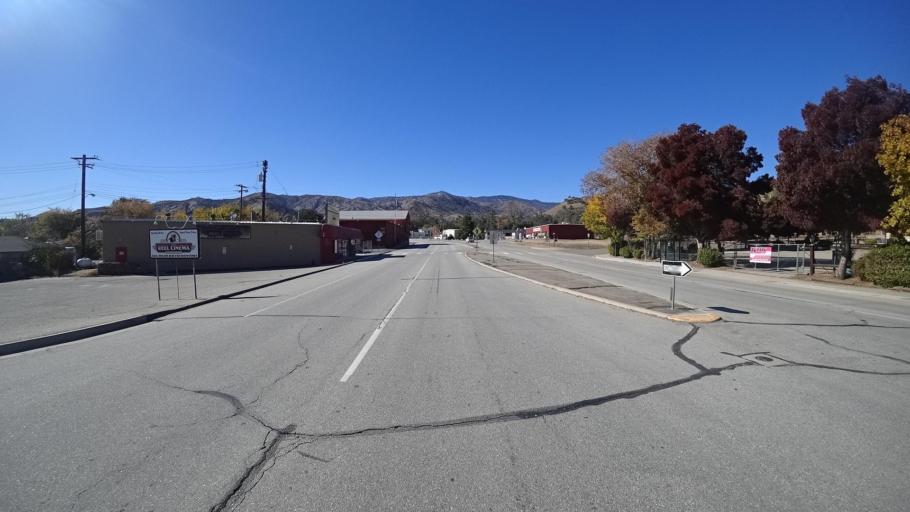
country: US
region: California
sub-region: Kern County
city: Wofford Heights
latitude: 35.7082
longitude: -118.4531
